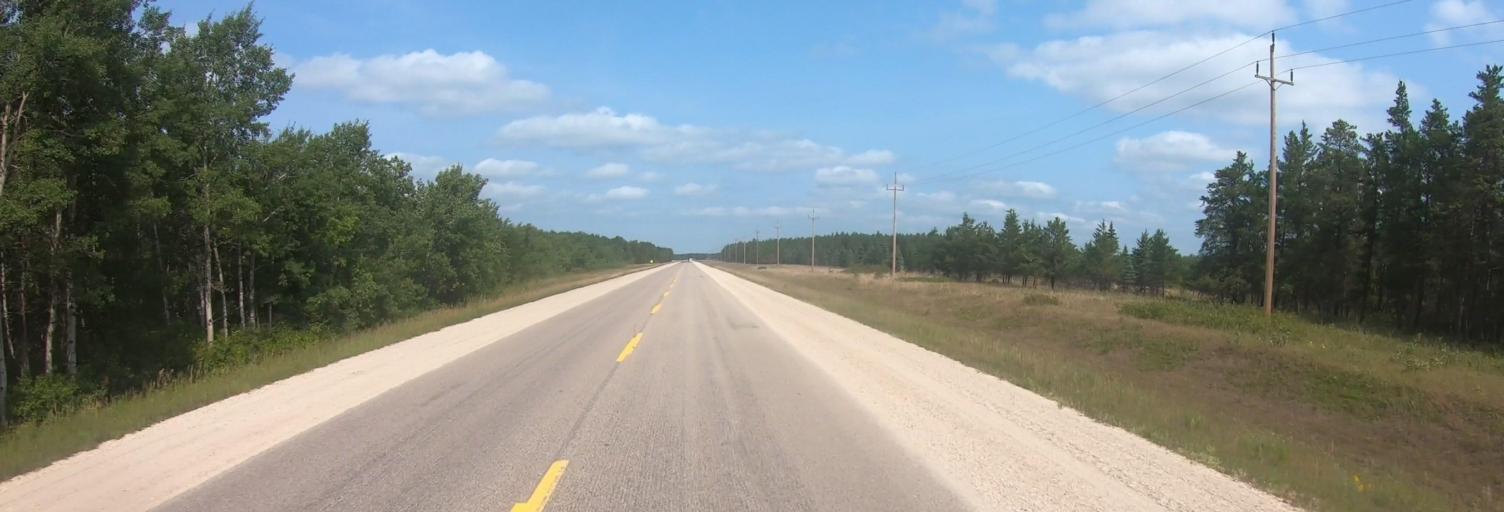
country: CA
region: Manitoba
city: La Broquerie
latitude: 49.2515
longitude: -96.3546
